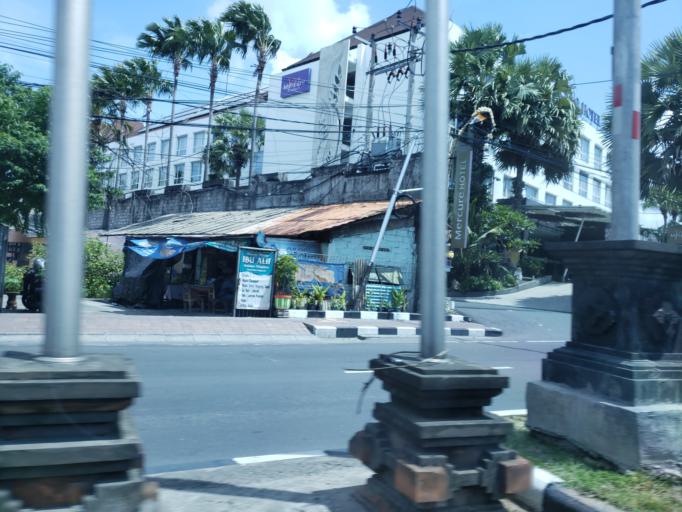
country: ID
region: Bali
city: Jabajero
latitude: -8.7270
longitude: 115.1802
